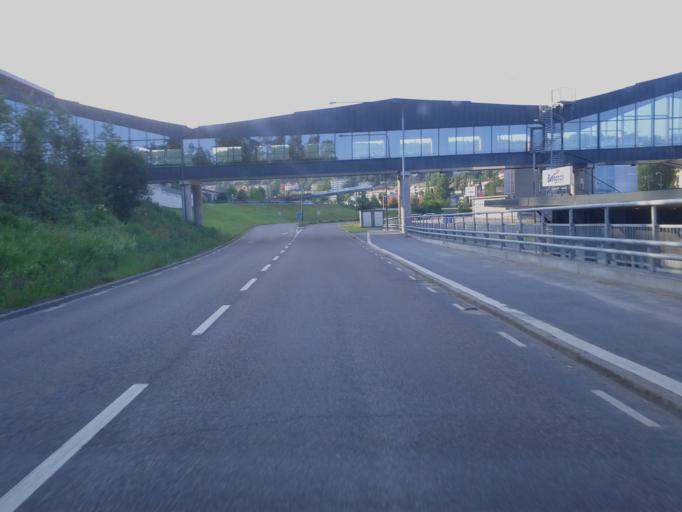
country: SE
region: Vaesternorrland
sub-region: OErnskoeldsviks Kommun
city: Ornskoldsvik
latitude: 63.2874
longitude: 18.7068
